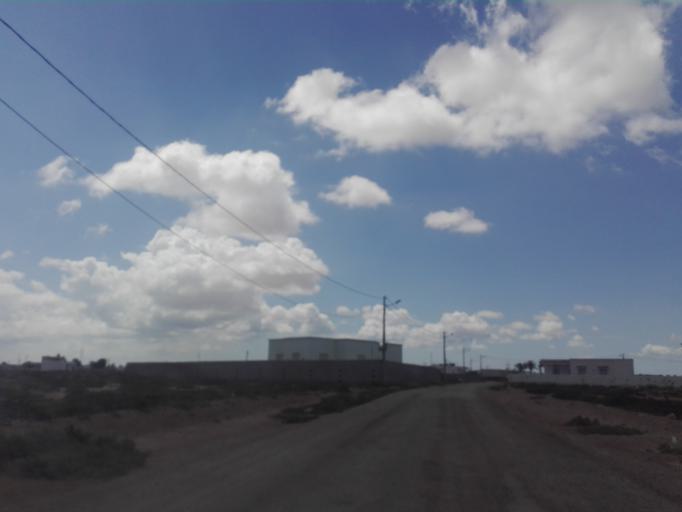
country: TN
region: Safaqis
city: Jabinyanah
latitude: 34.8238
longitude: 11.2537
